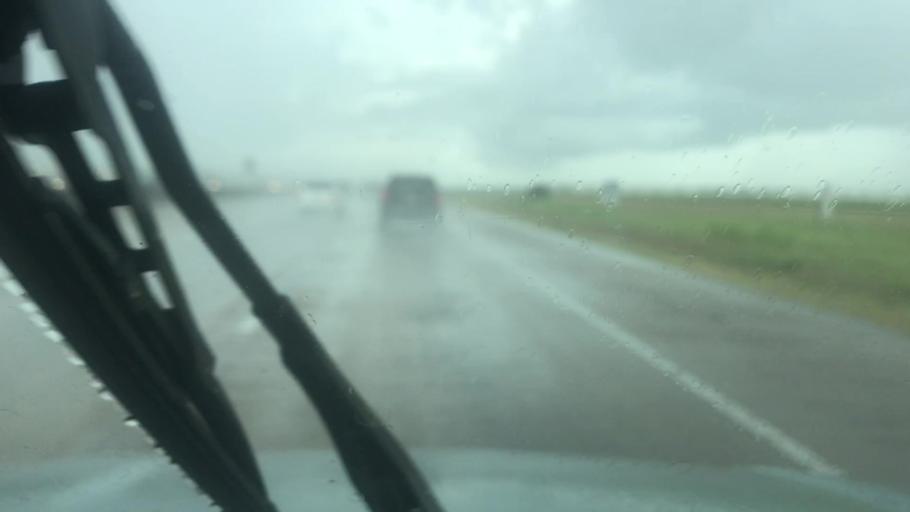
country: US
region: Texas
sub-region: Waller County
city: Brookshire
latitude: 29.7774
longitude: -95.9016
